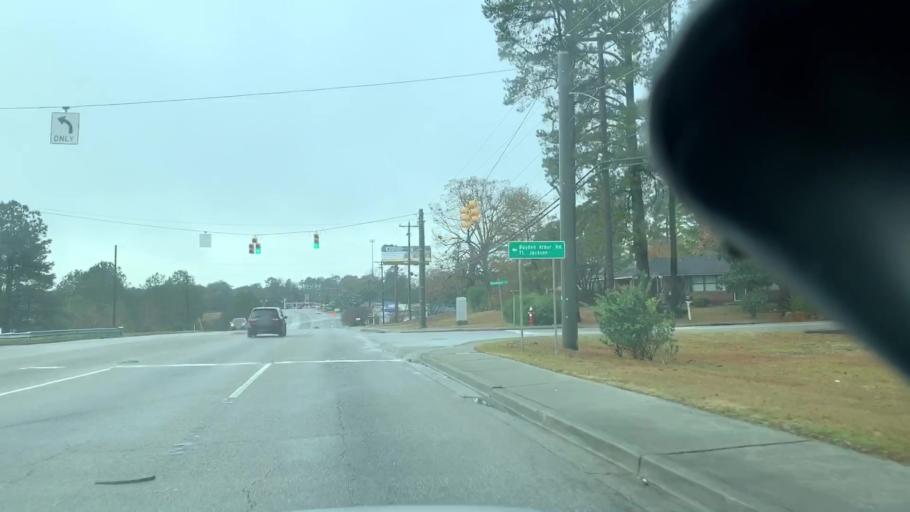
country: US
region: South Carolina
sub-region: Richland County
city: Woodfield
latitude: 34.0452
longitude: -80.9334
